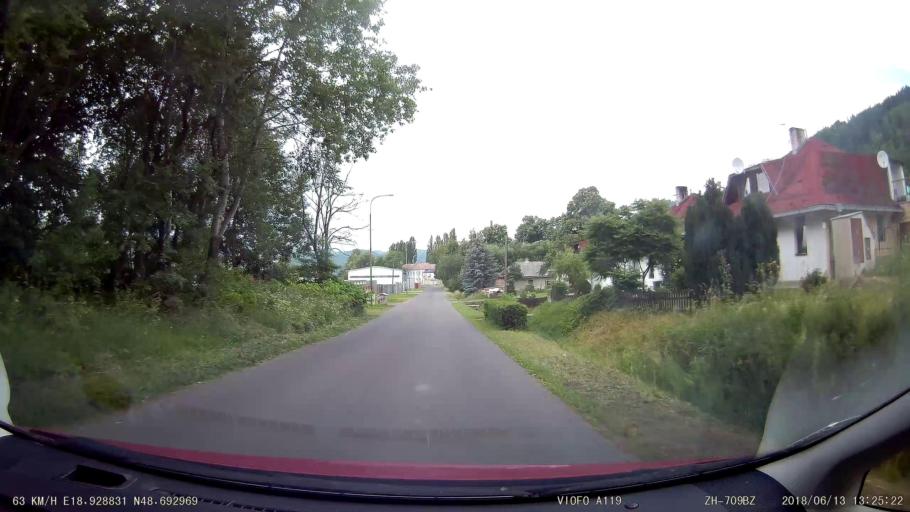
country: SK
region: Banskobystricky
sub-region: Okres Ziar nad Hronom
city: Kremnica
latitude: 48.6930
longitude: 18.9288
